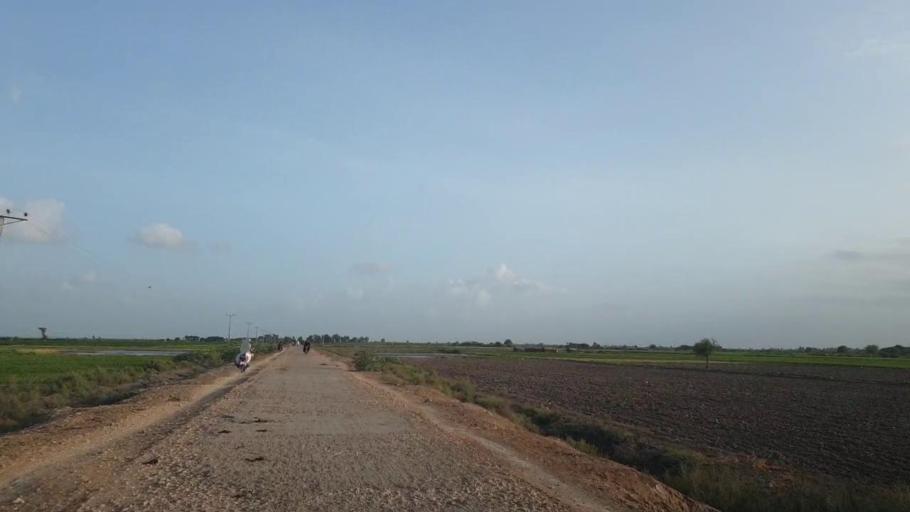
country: PK
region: Sindh
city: Kadhan
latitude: 24.6261
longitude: 69.1158
